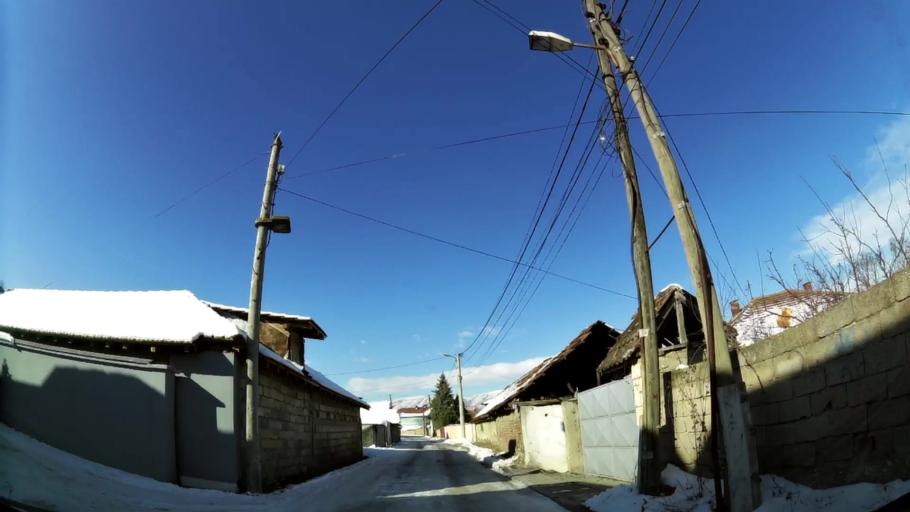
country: MK
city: Ljubin
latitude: 42.0023
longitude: 21.3134
